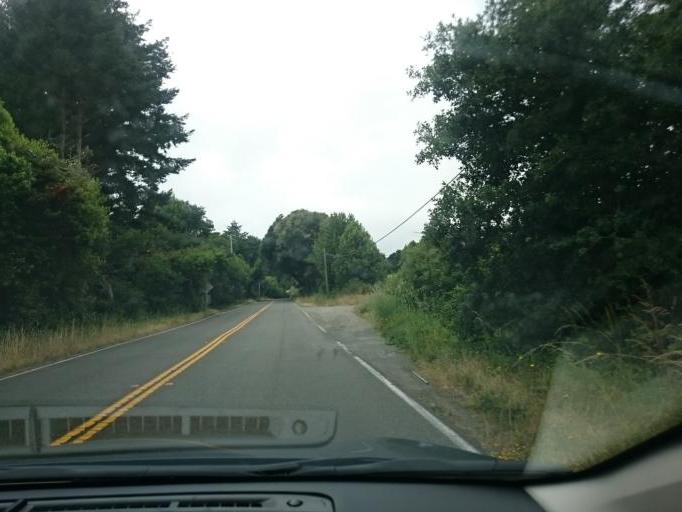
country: US
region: California
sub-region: Marin County
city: Lagunitas-Forest Knolls
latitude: 38.0000
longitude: -122.7564
